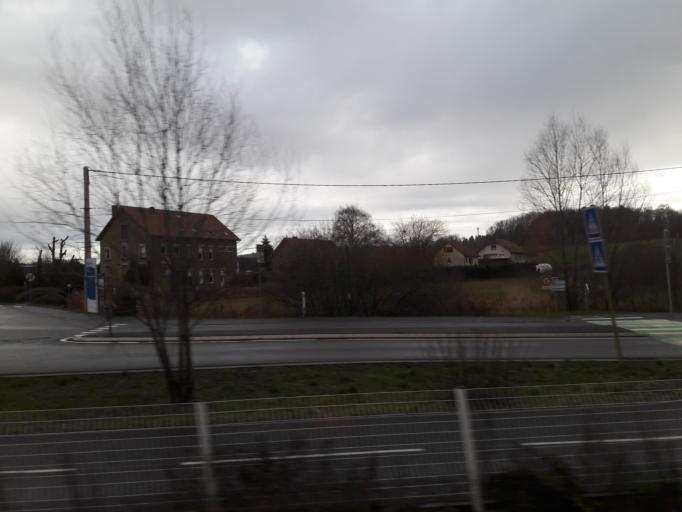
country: FR
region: Franche-Comte
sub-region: Territoire de Belfort
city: Morvillars
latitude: 47.5553
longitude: 6.9276
